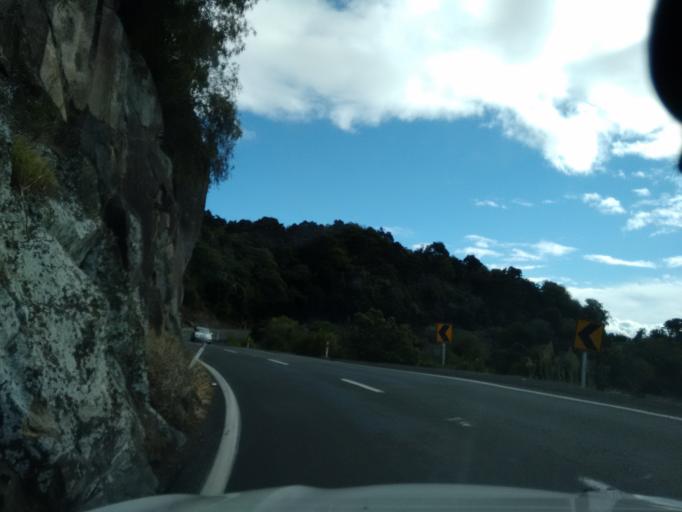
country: NZ
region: Waikato
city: Turangi
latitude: -38.8830
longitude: 175.9689
